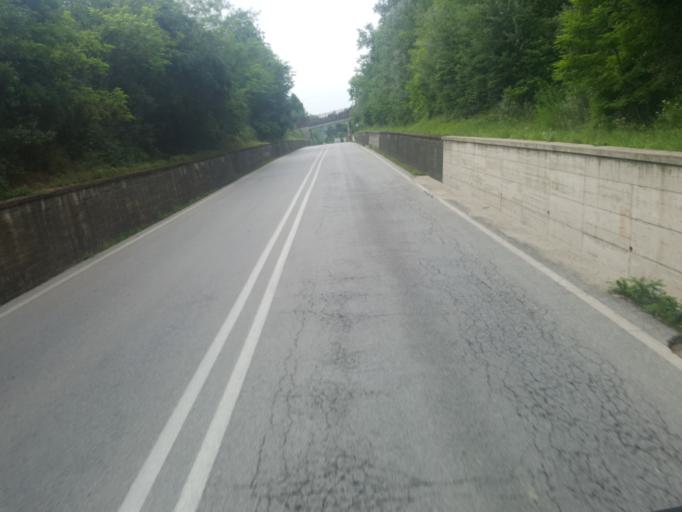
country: IT
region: Piedmont
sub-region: Provincia di Cuneo
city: Canale
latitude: 44.7984
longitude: 7.9823
